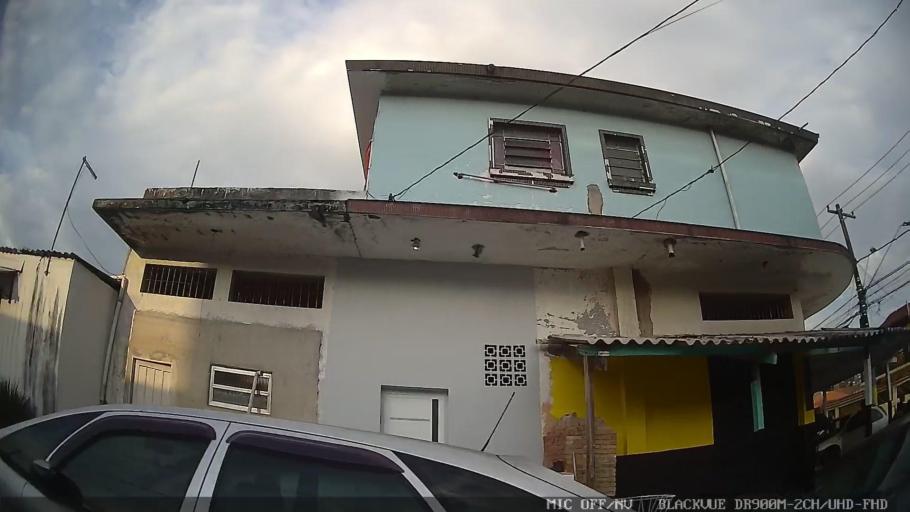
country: BR
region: Sao Paulo
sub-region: Cubatao
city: Cubatao
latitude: -23.8944
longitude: -46.4298
